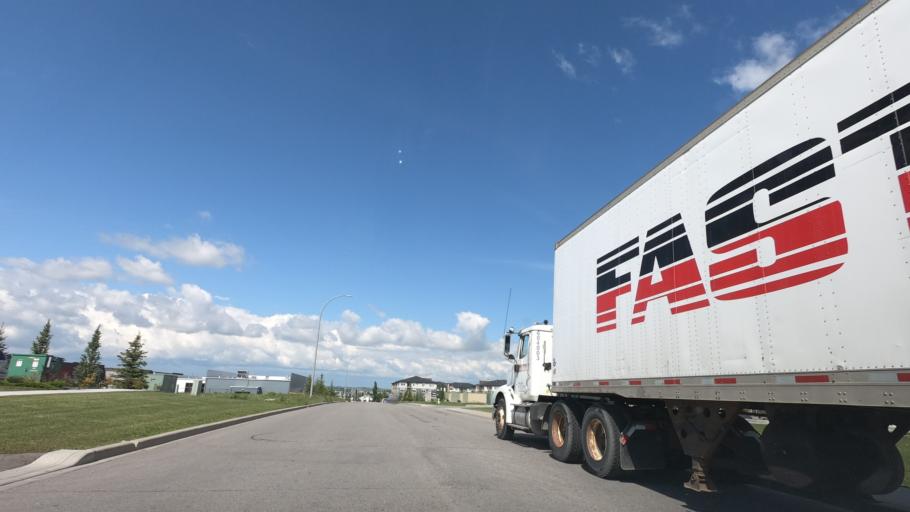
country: CA
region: Alberta
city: Airdrie
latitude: 51.3040
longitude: -114.0080
